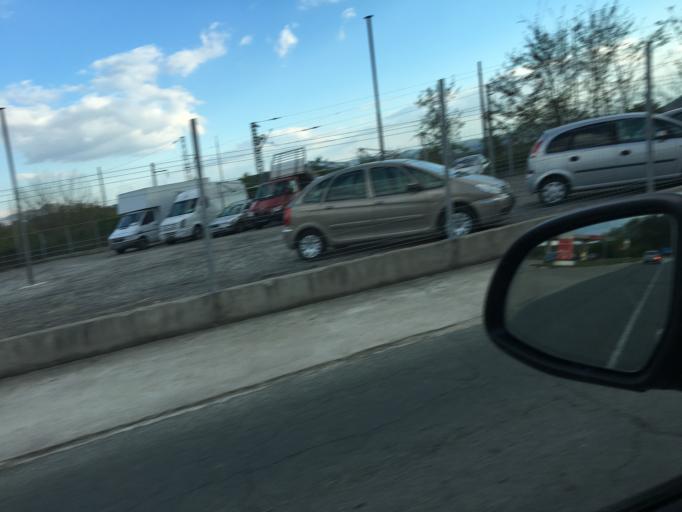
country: BG
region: Plovdiv
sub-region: Obshtina Karlovo
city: Kalofer
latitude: 42.6005
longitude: 24.8992
